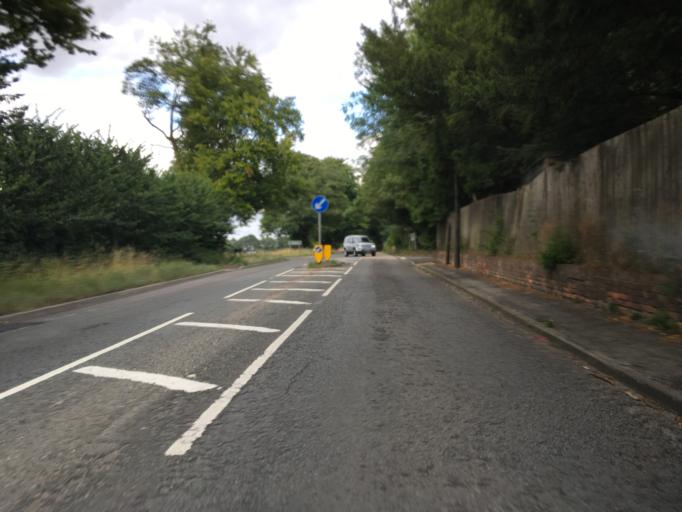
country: GB
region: England
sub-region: Hampshire
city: Kings Worthy
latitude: 51.0929
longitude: -1.2926
